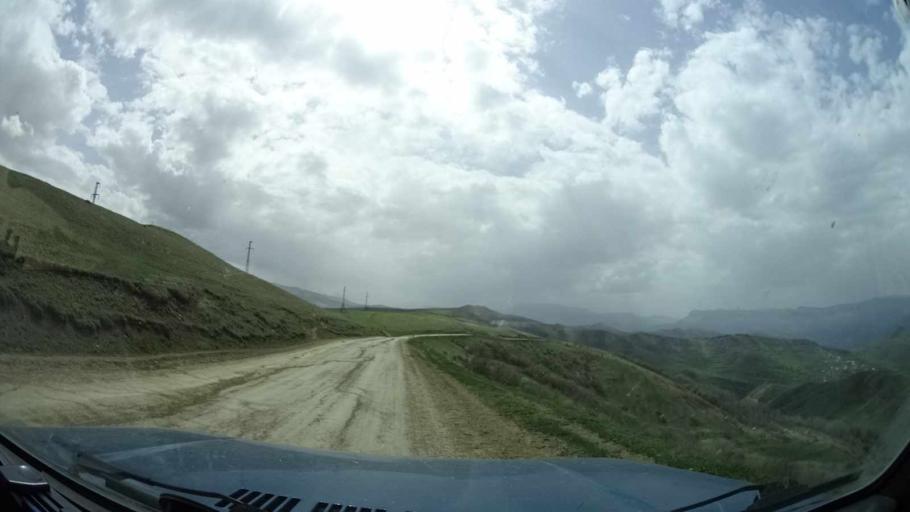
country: RU
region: Dagestan
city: Kubachi
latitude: 42.0877
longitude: 47.5777
